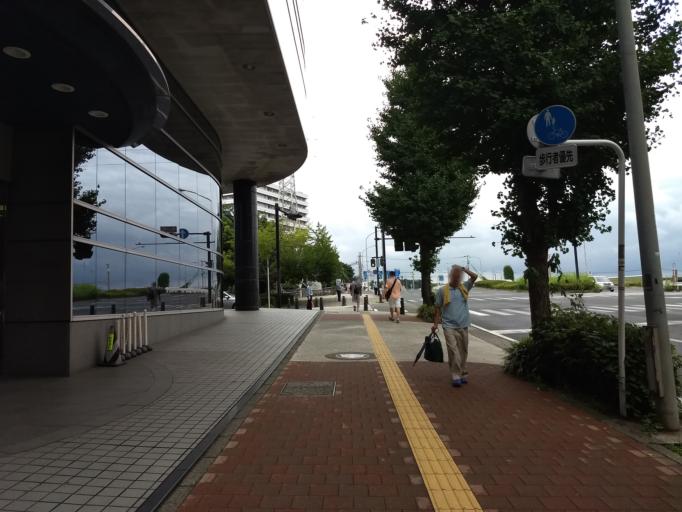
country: JP
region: Kanagawa
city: Yokohama
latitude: 35.5112
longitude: 139.6150
